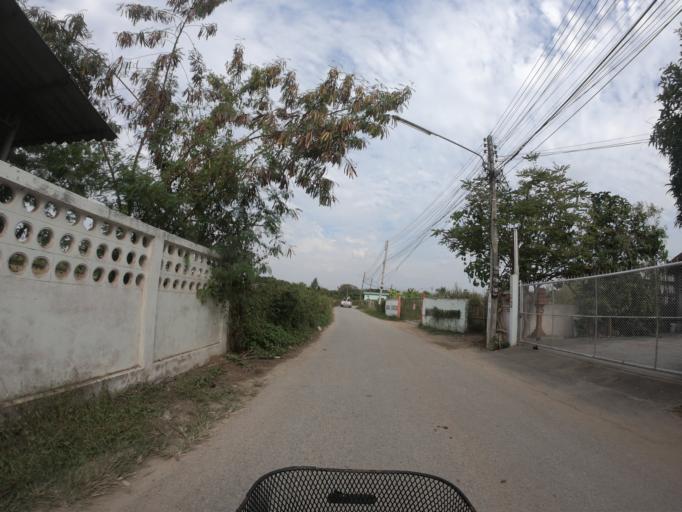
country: TH
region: Chiang Mai
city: San Sai
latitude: 18.8002
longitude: 99.0491
